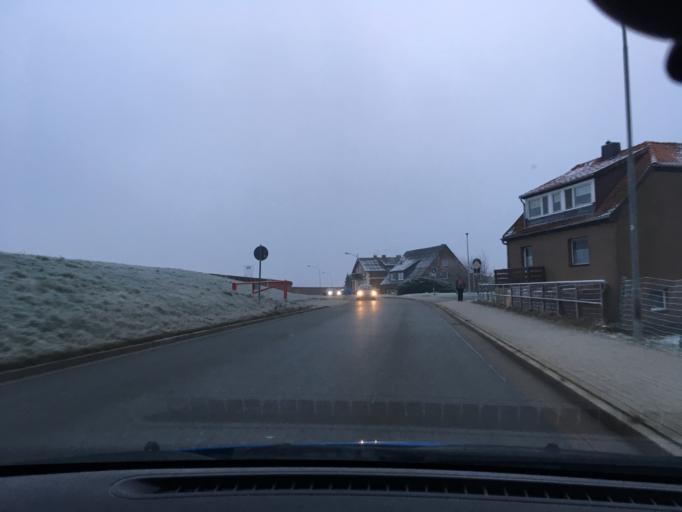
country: DE
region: Lower Saxony
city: Stelle
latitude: 53.4339
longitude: 10.0977
